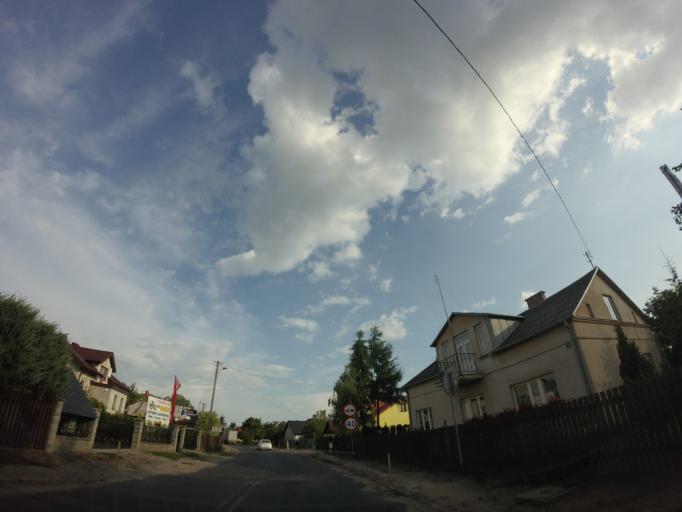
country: PL
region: Lublin Voivodeship
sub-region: Powiat lubartowski
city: Przytoczno
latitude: 51.6143
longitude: 22.2735
